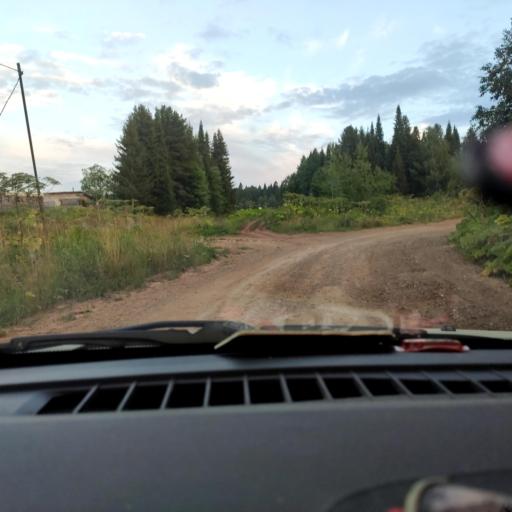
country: RU
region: Perm
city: Kultayevo
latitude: 57.8206
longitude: 55.9998
